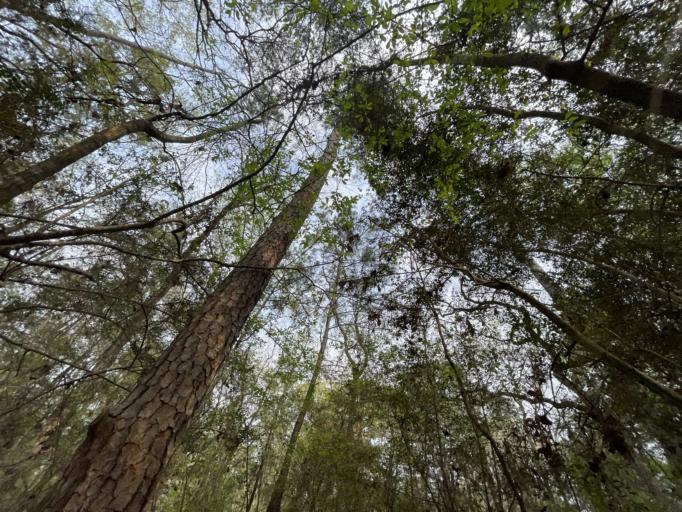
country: US
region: Texas
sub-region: Walker County
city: Huntsville
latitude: 30.6595
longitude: -95.4850
